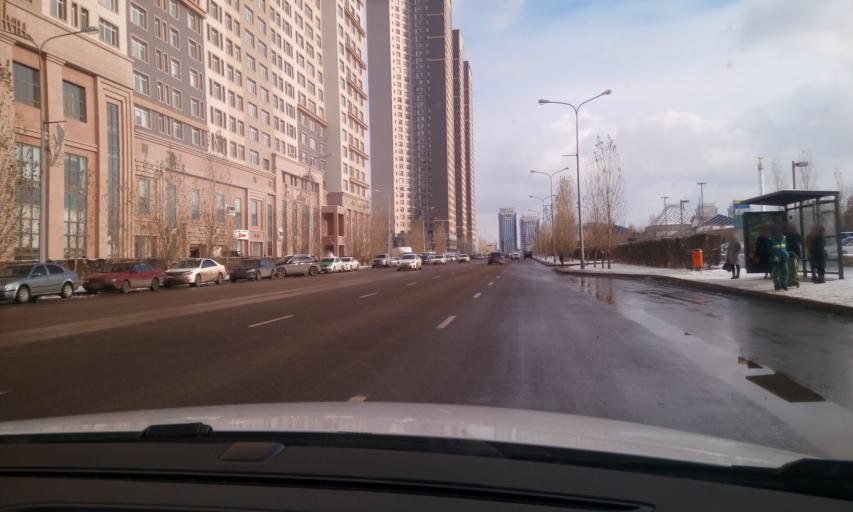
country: KZ
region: Astana Qalasy
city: Astana
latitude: 51.1267
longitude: 71.4614
